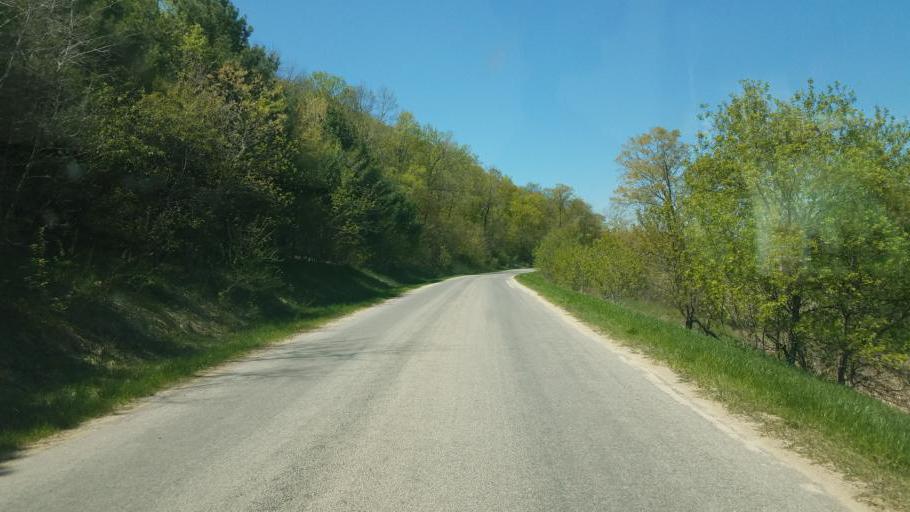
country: US
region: Wisconsin
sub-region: Vernon County
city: Hillsboro
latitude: 43.6247
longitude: -90.4761
